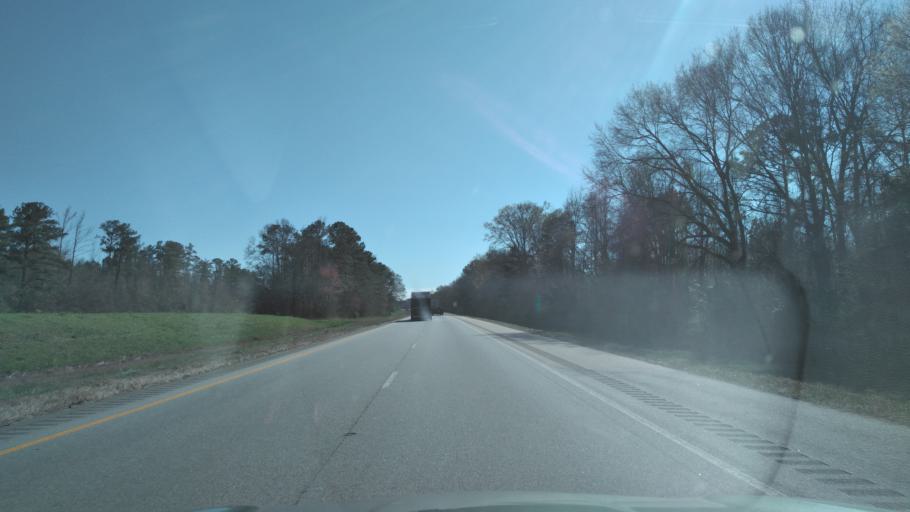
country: US
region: Alabama
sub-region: Lowndes County
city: Fort Deposit
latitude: 31.9791
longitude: -86.5328
